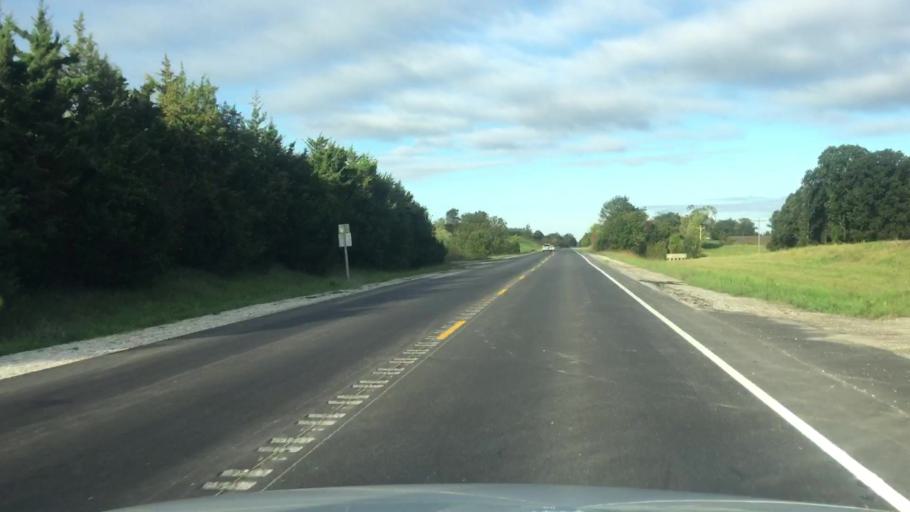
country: US
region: Missouri
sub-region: Boone County
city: Columbia
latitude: 38.9892
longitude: -92.4972
